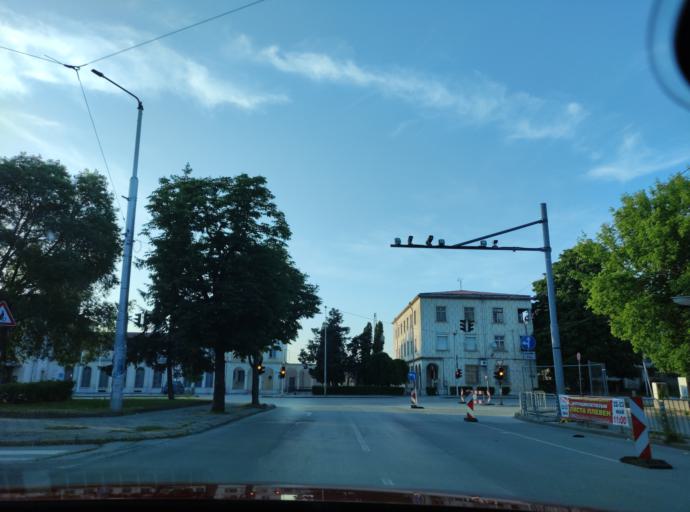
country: BG
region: Pleven
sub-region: Obshtina Pleven
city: Pleven
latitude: 43.4200
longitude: 24.6152
